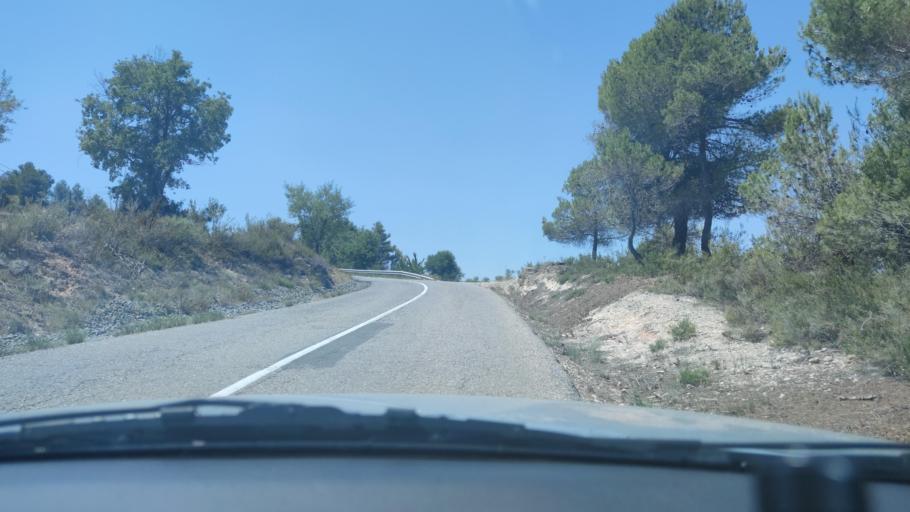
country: ES
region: Catalonia
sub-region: Provincia de Tarragona
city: Vallclara
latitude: 41.3944
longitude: 0.9528
